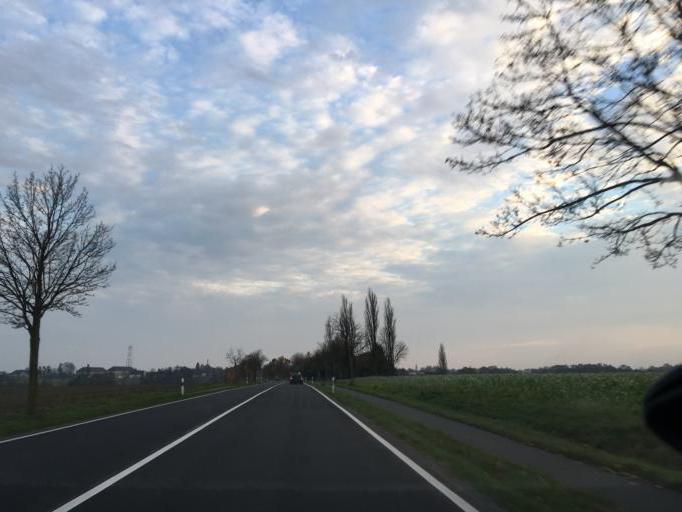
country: DE
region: Lower Saxony
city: Celle
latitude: 52.6469
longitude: 10.0733
